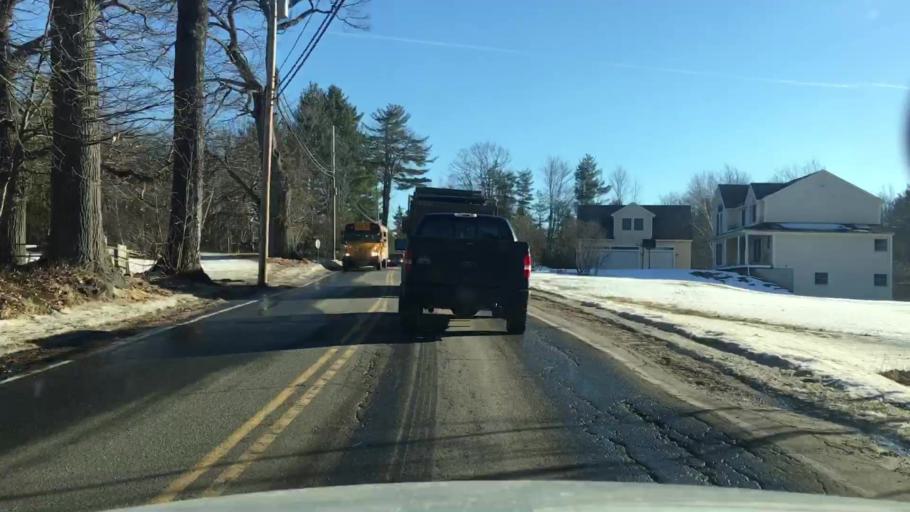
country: US
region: Maine
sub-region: Cumberland County
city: Westbrook
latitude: 43.7138
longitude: -70.3597
